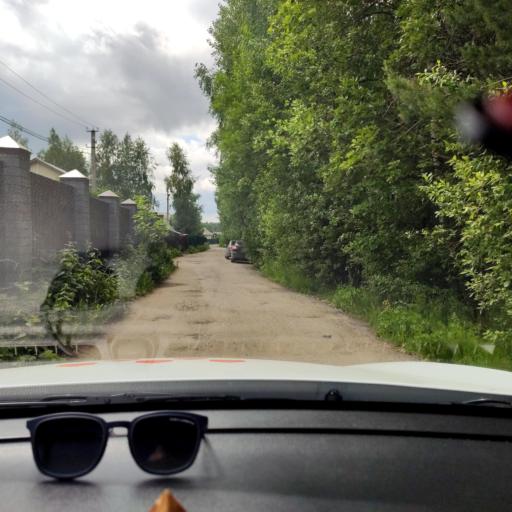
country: RU
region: Tatarstan
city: Vysokaya Gora
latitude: 55.9287
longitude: 49.1624
